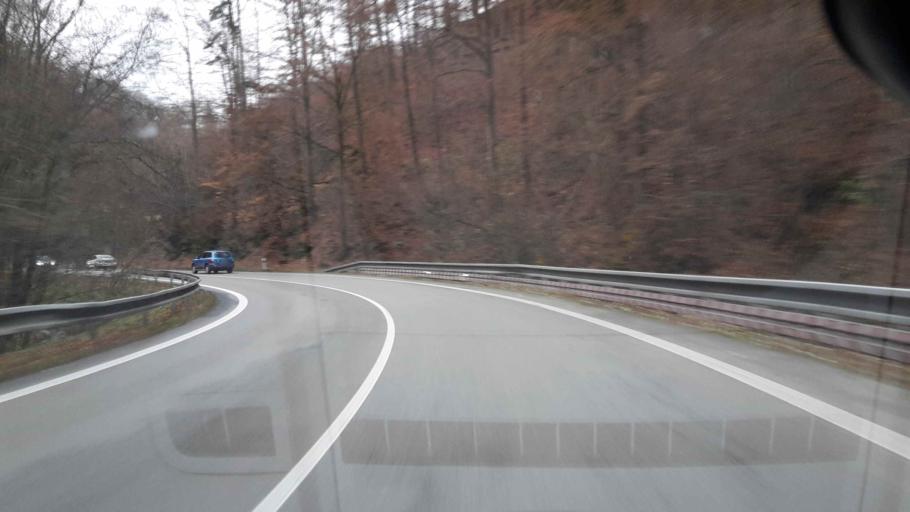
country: CZ
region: South Moravian
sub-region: Okres Blansko
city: Adamov
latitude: 49.3239
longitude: 16.6261
